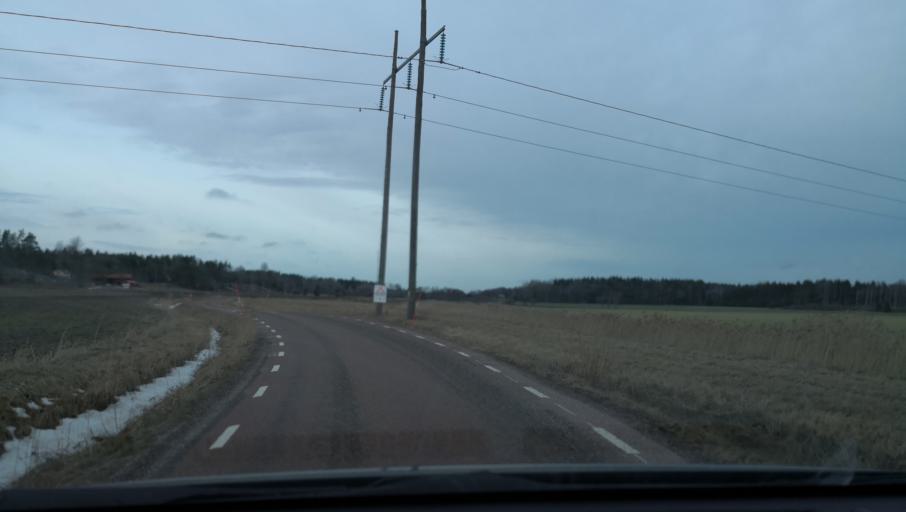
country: SE
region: Vaestmanland
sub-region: Vasteras
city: Skultuna
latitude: 59.6000
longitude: 16.4131
